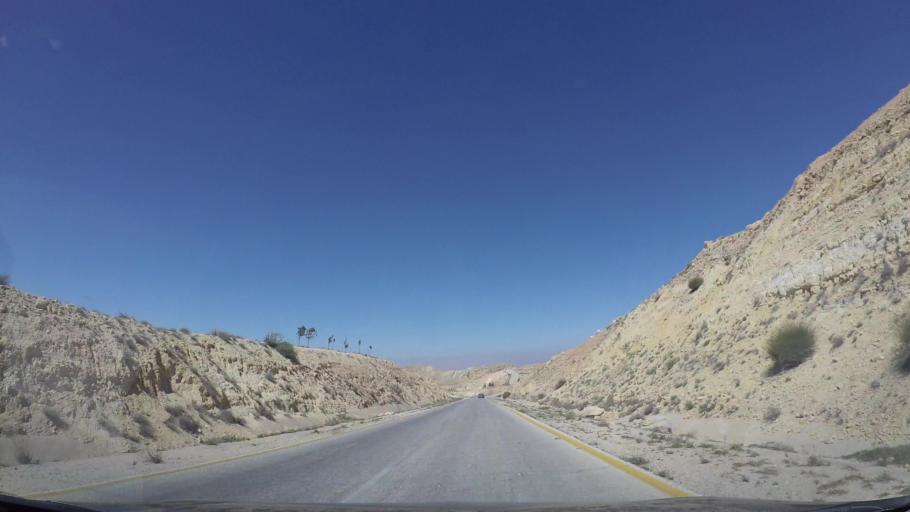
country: JO
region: Tafielah
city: At Tafilah
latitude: 30.8509
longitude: 35.5559
